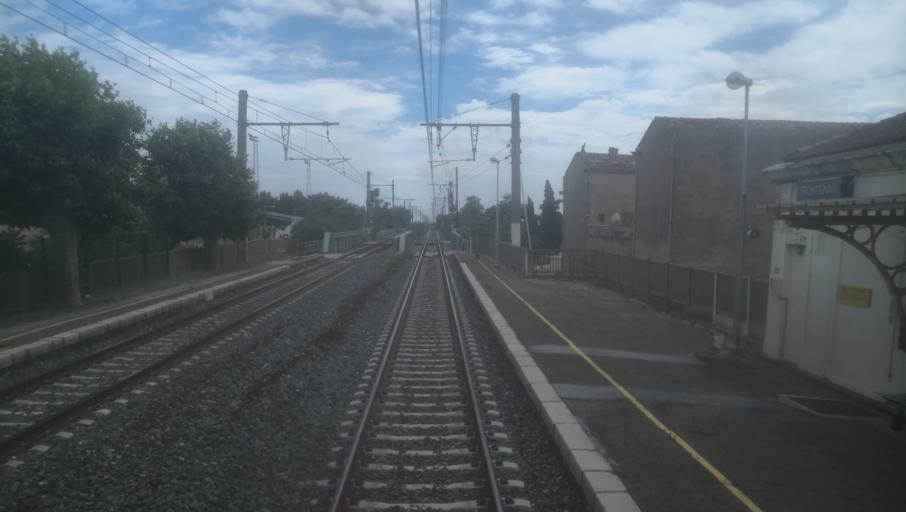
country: FR
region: Languedoc-Roussillon
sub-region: Departement de l'Herault
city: Frontignan
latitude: 43.4449
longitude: 3.7589
